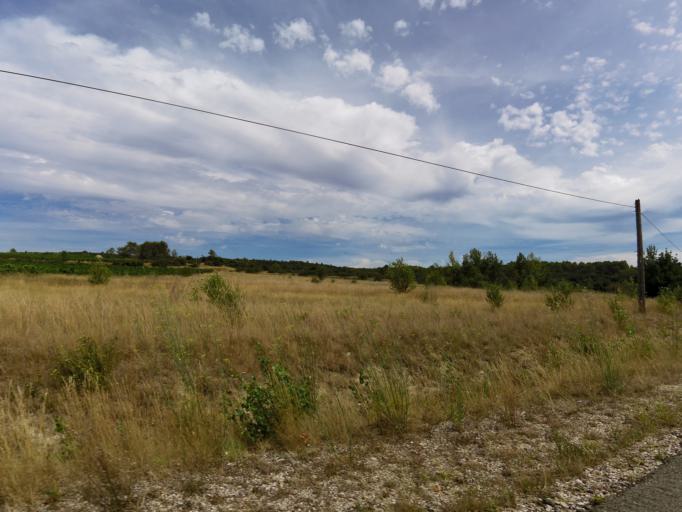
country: FR
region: Languedoc-Roussillon
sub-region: Departement du Gard
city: Saint-Mamert-du-Gard
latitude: 43.8411
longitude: 4.1417
